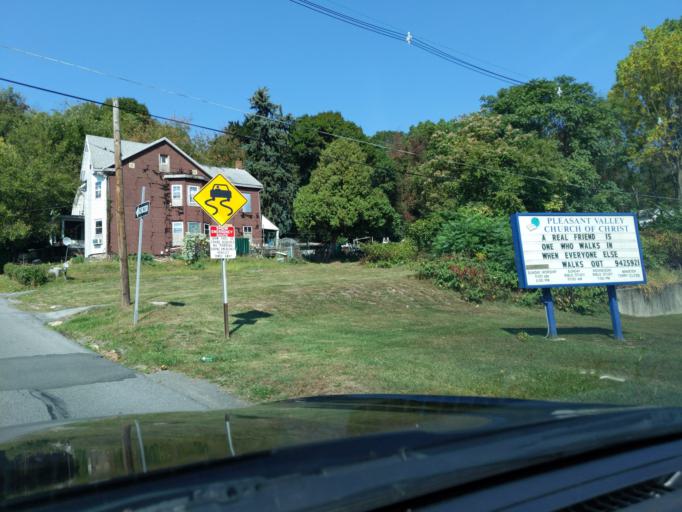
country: US
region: Pennsylvania
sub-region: Blair County
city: Altoona
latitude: 40.5121
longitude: -78.3835
